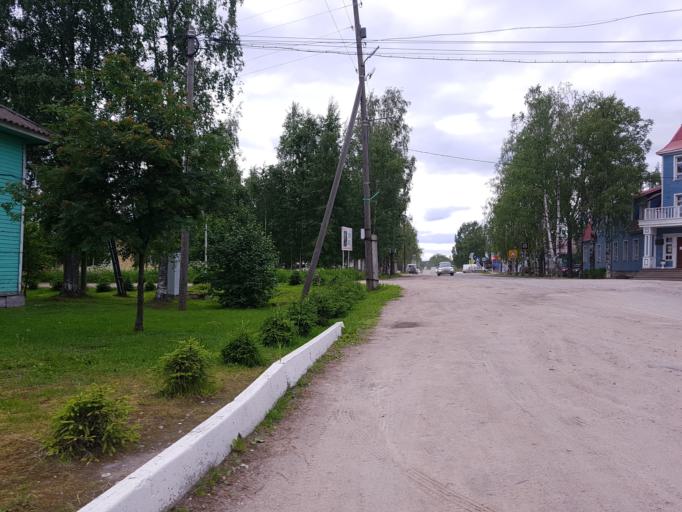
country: RU
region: Republic of Karelia
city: Kalevala
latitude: 65.1967
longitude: 31.1819
